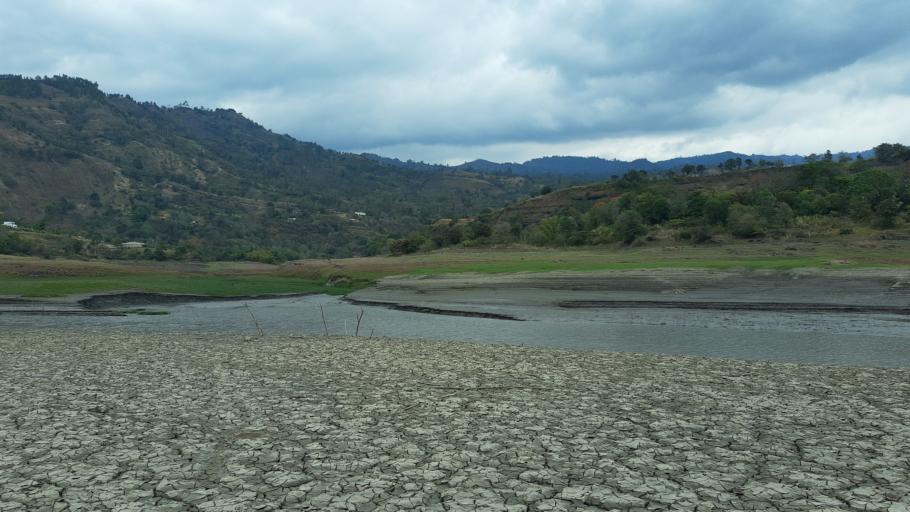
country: CO
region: Boyaca
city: Garagoa
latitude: 5.0113
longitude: -73.3645
